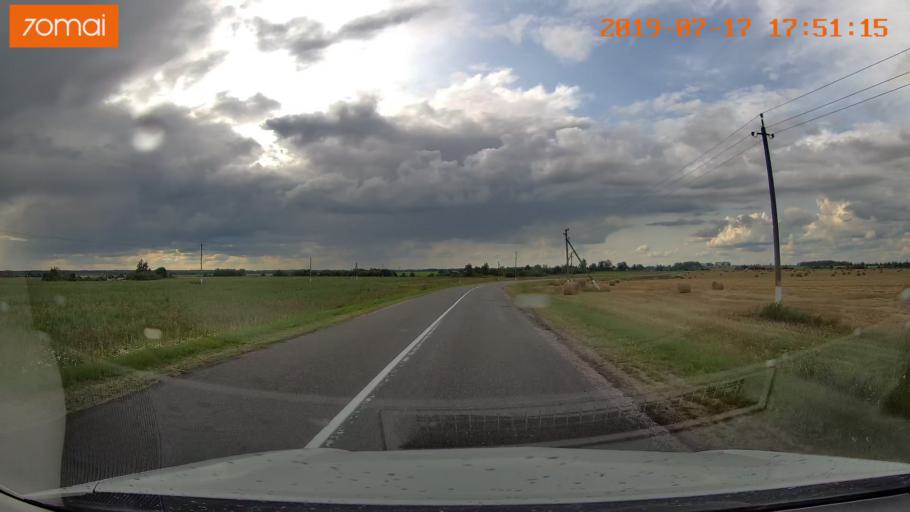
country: BY
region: Mogilev
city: Hlusha
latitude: 53.1498
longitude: 28.7901
